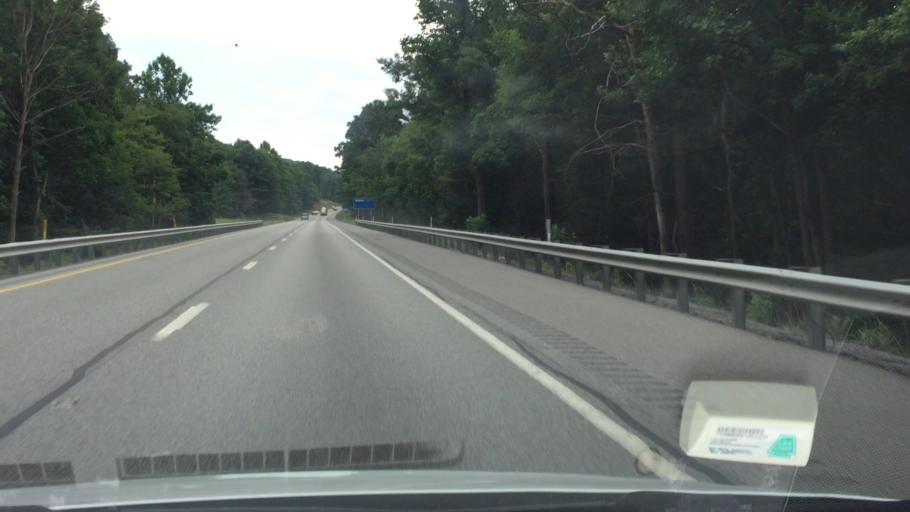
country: US
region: Pennsylvania
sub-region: Bedford County
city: Earlston
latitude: 39.9058
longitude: -78.2385
